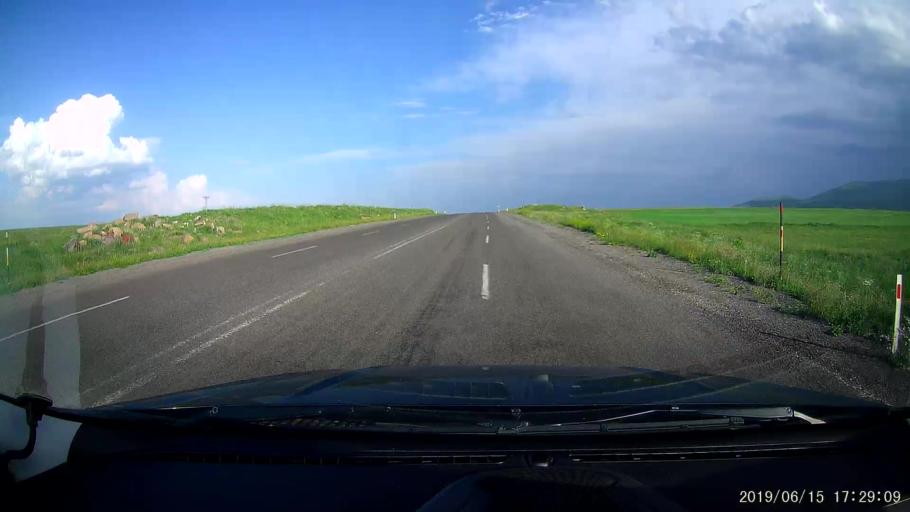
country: TR
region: Kars
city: Basgedikler
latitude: 40.5917
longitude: 43.4492
